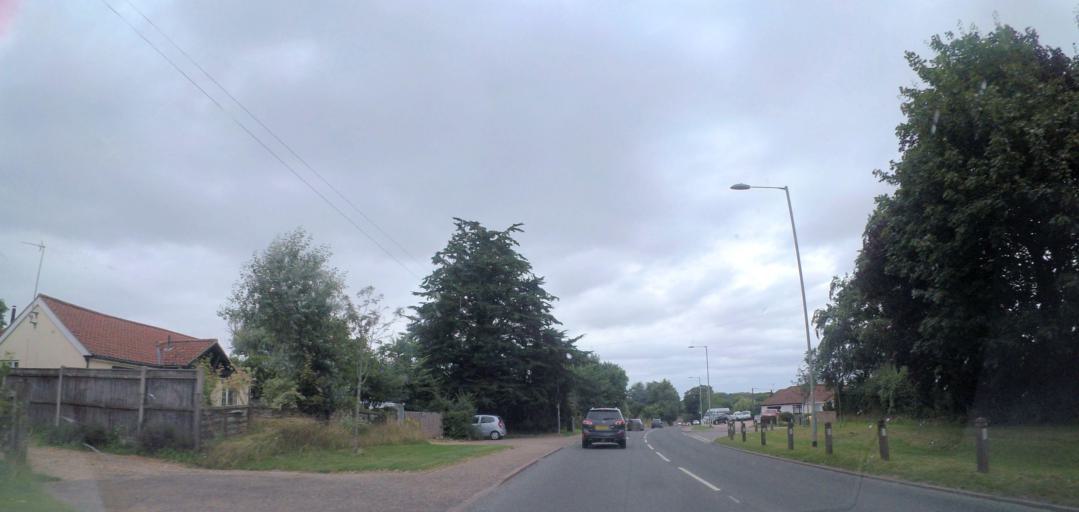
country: GB
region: England
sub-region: Norfolk
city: Coltishall
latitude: 52.7228
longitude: 1.3502
